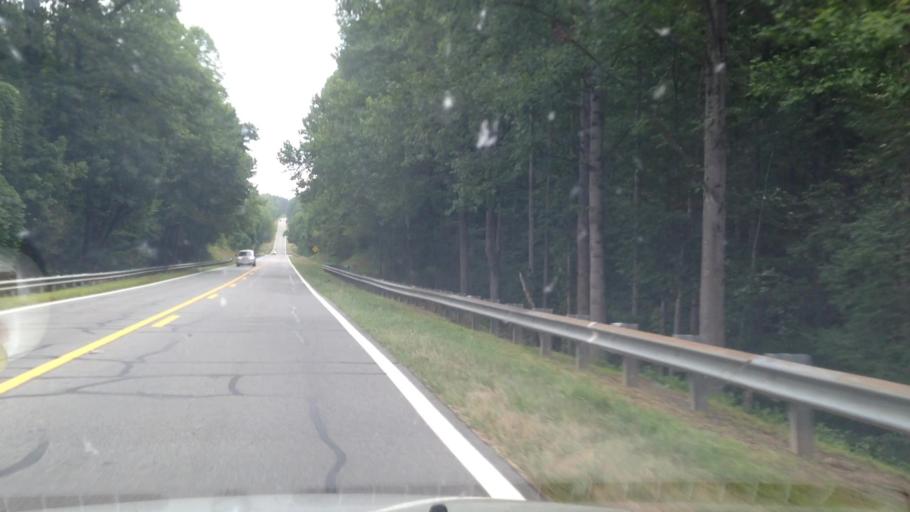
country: US
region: North Carolina
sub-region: Rockingham County
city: Madison
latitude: 36.3792
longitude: -79.8808
